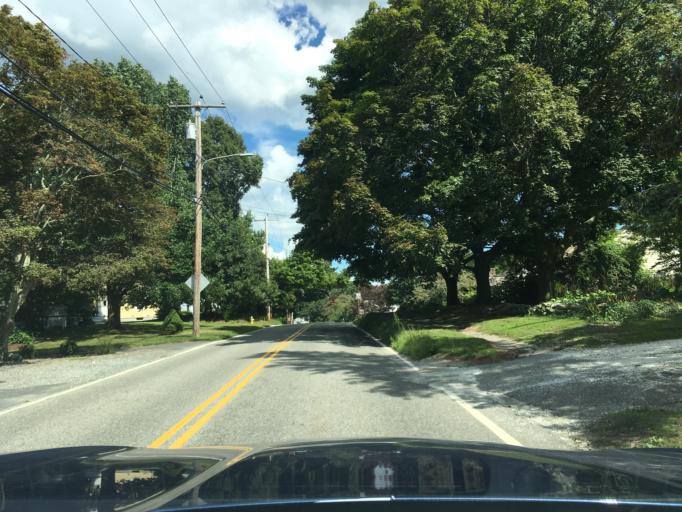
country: US
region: Rhode Island
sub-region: Bristol County
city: Barrington
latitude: 41.7389
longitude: -71.3288
